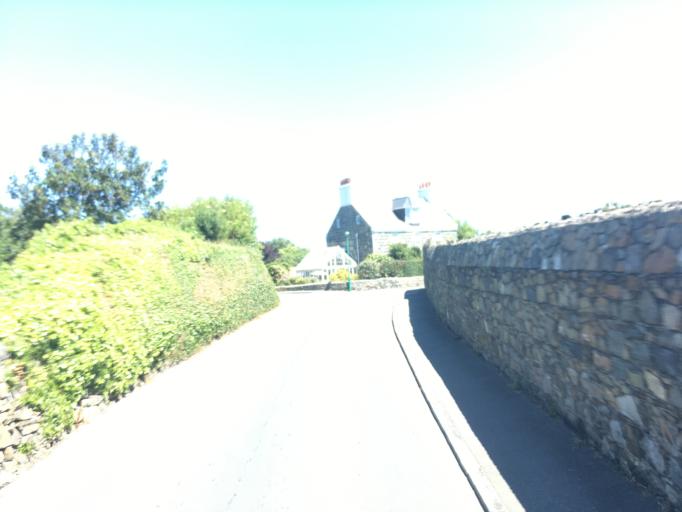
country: GG
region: St Peter Port
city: Saint Peter Port
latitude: 49.4884
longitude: -2.5150
